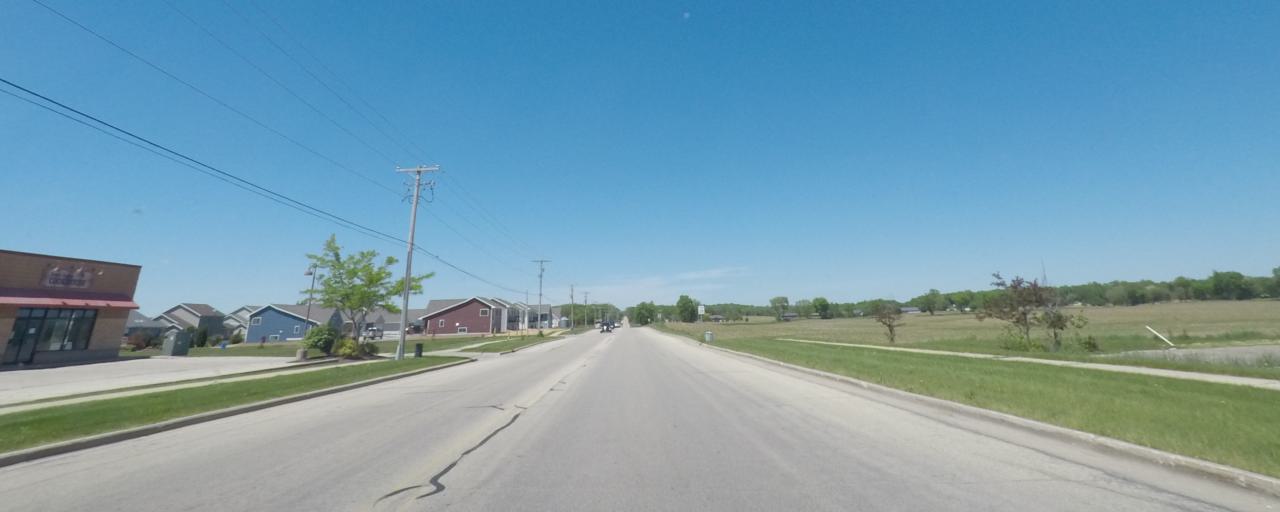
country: US
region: Wisconsin
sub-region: Green County
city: Brooklyn
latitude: 42.8589
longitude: -89.3691
